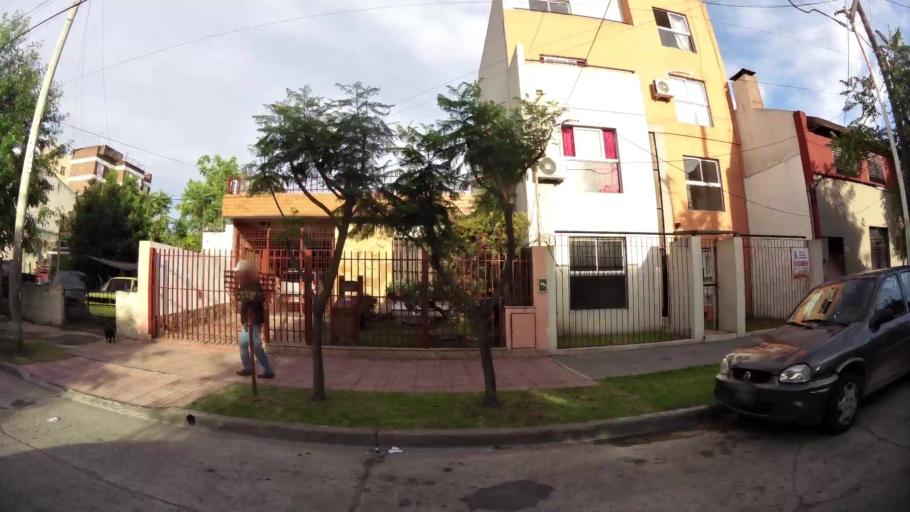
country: AR
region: Buenos Aires
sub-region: Partido de Moron
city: Moron
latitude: -34.6591
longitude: -58.6215
